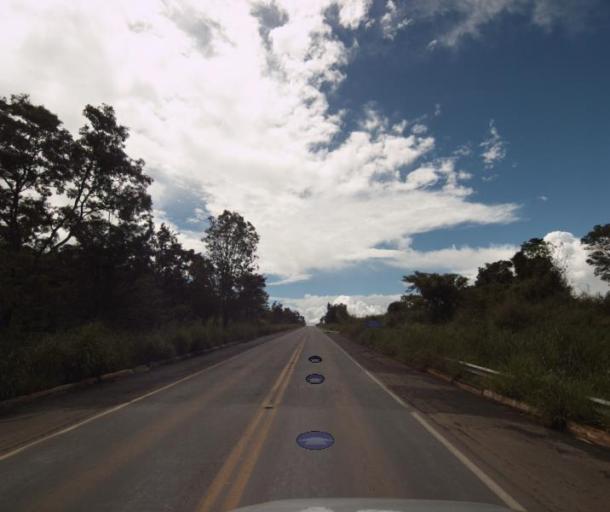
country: BR
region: Goias
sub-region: Uruacu
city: Uruacu
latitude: -14.1901
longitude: -49.1275
